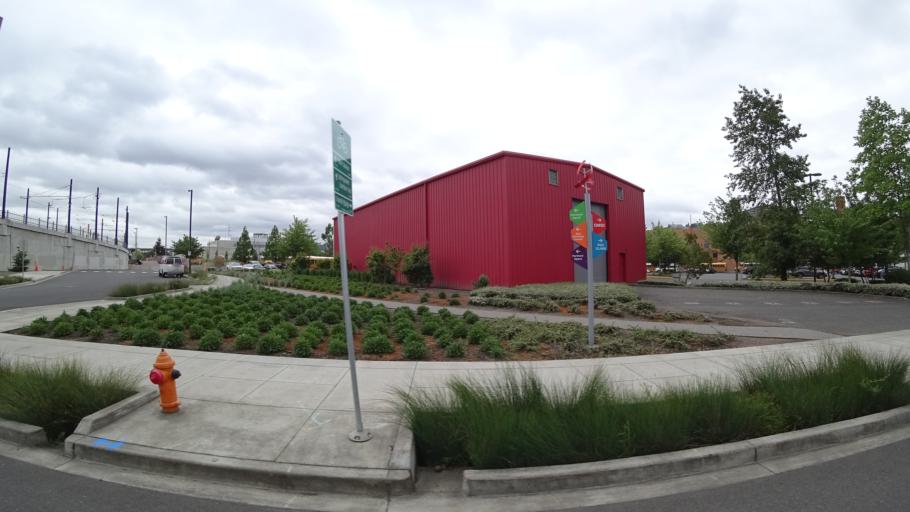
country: US
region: Oregon
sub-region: Multnomah County
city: Portland
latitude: 45.5082
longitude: -122.6634
